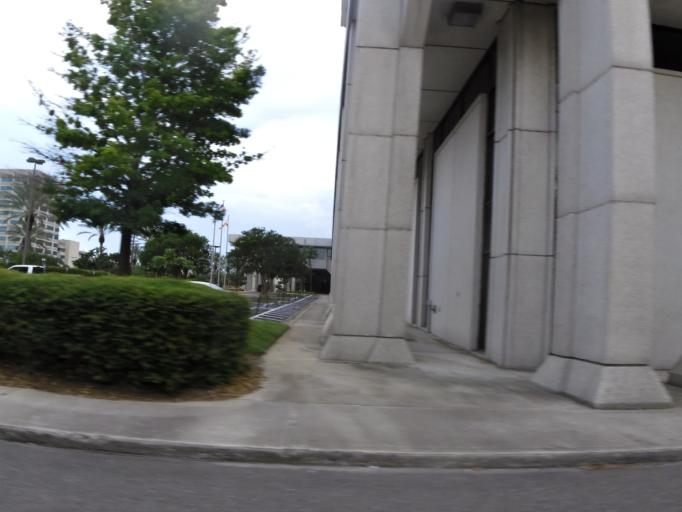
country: US
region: Florida
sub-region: Duval County
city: Jacksonville
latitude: 30.3206
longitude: -81.6753
